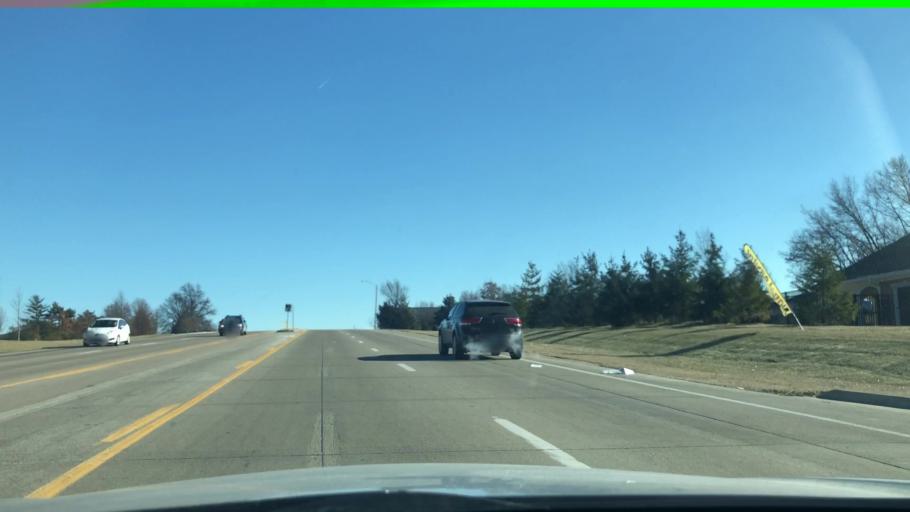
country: US
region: Missouri
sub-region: Boone County
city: Columbia
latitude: 38.9556
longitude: -92.3903
